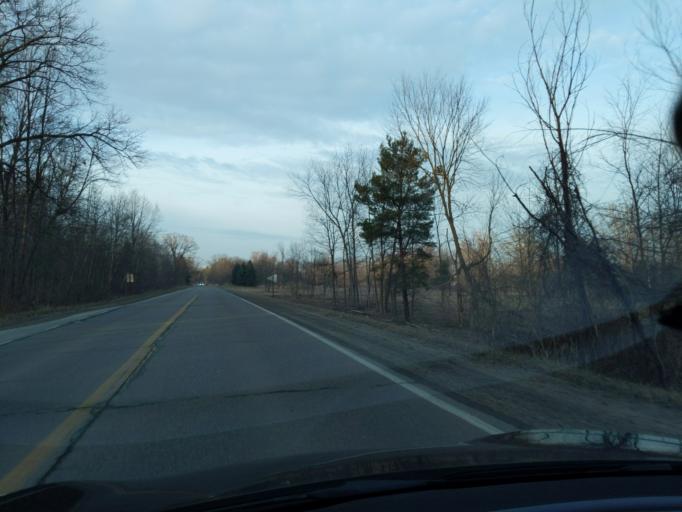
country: US
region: Michigan
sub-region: Livingston County
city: Brighton
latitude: 42.6071
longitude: -83.7482
